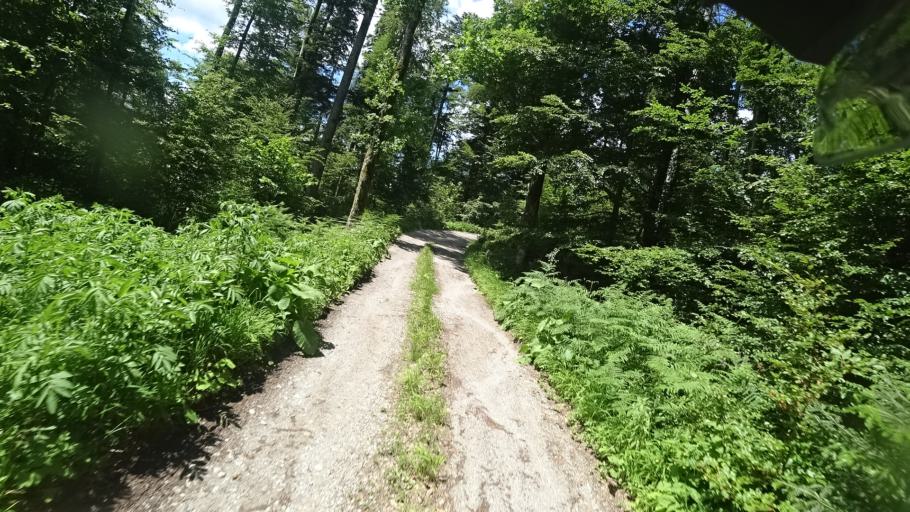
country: SI
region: Osilnica
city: Osilnica
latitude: 45.4760
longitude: 14.7364
